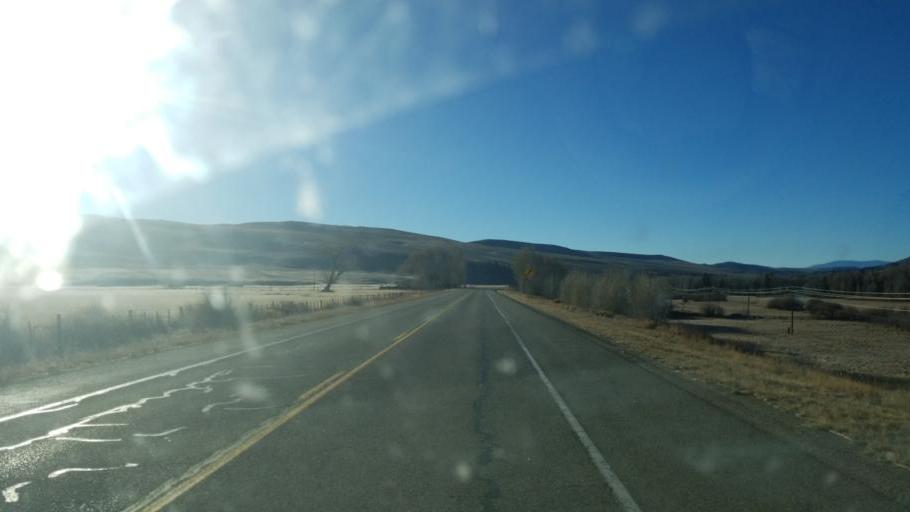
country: US
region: Colorado
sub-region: Gunnison County
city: Crested Butte
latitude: 38.7349
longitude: -106.8537
